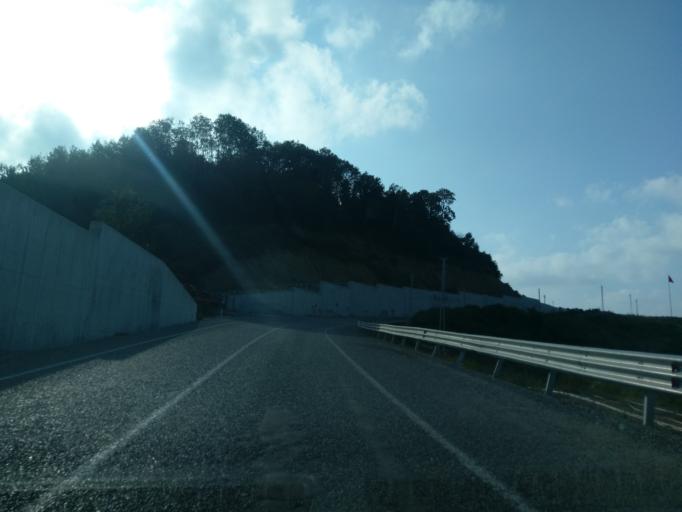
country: TR
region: Sinop
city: Helaldi
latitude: 41.9492
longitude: 34.3899
